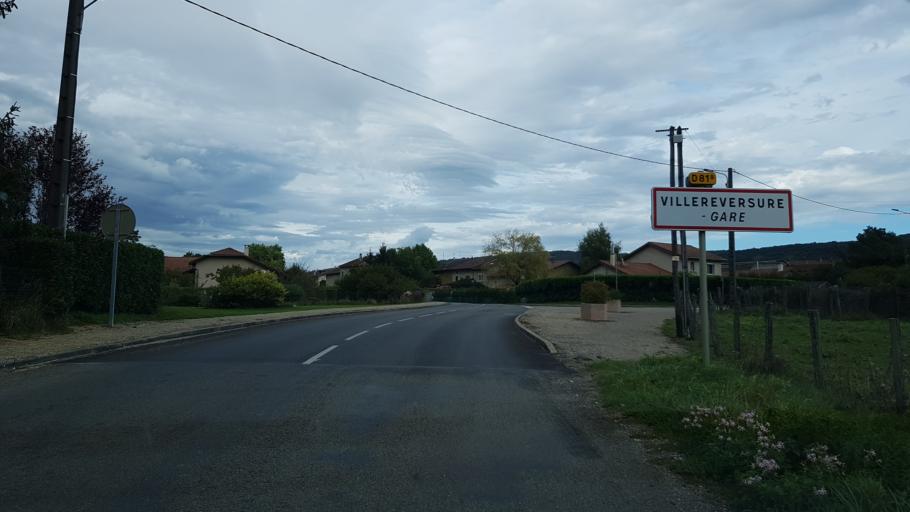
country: FR
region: Rhone-Alpes
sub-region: Departement de l'Ain
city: Villereversure
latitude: 46.1875
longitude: 5.3911
